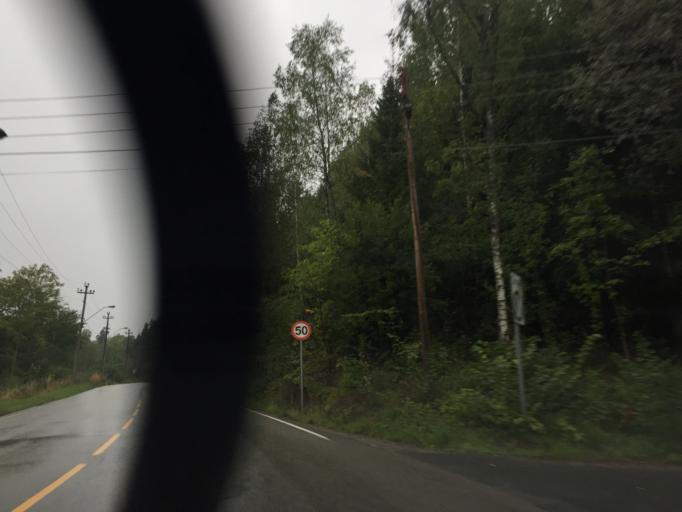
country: NO
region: Akershus
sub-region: Baerum
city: Lysaker
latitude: 59.9701
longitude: 10.6383
